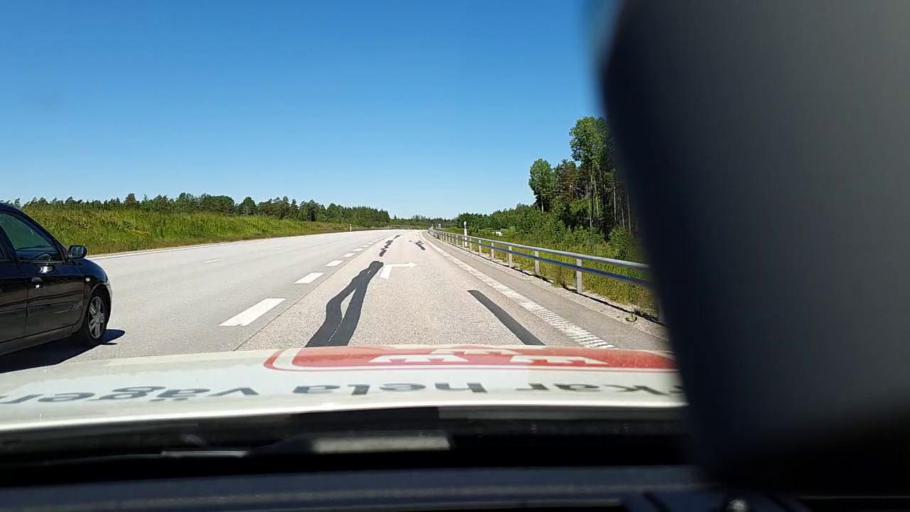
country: SE
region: Uppsala
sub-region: Osthammars Kommun
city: Bjorklinge
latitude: 60.0093
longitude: 17.6257
